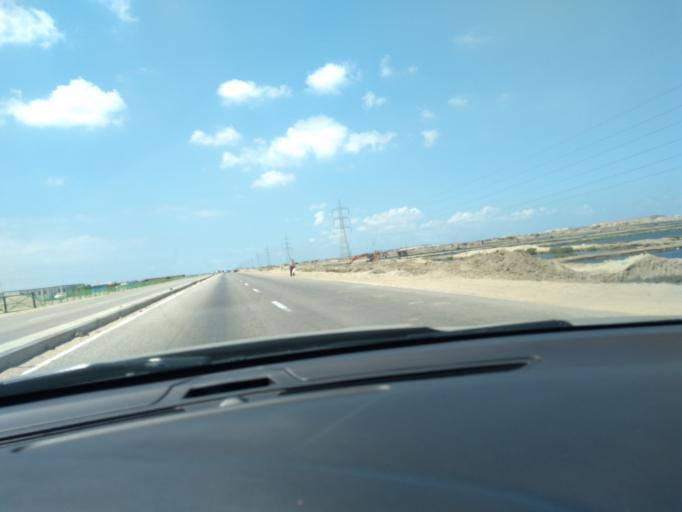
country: EG
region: Muhafazat Bur Sa`id
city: Port Said
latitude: 31.3090
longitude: 32.1329
